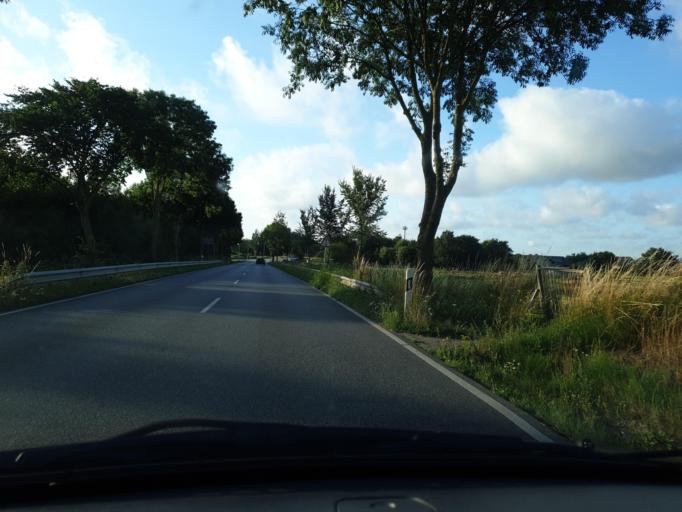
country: DE
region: Schleswig-Holstein
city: Busumer Deichhausen
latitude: 54.1330
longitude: 8.8751
